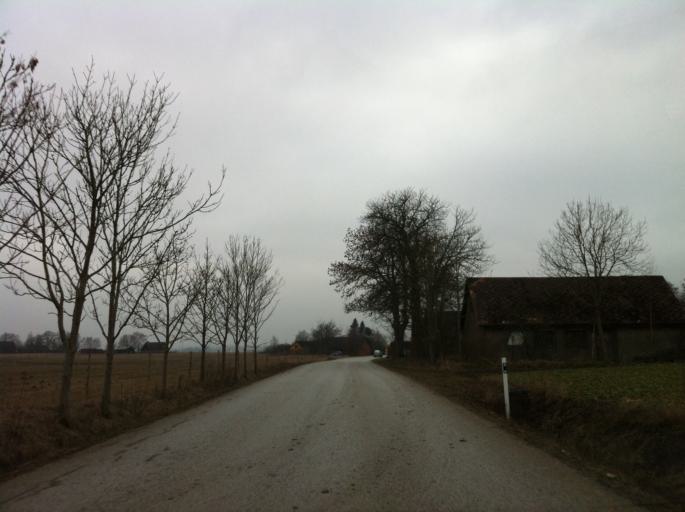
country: SE
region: Skane
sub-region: Svalovs Kommun
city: Svaloev
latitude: 55.9423
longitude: 13.0268
